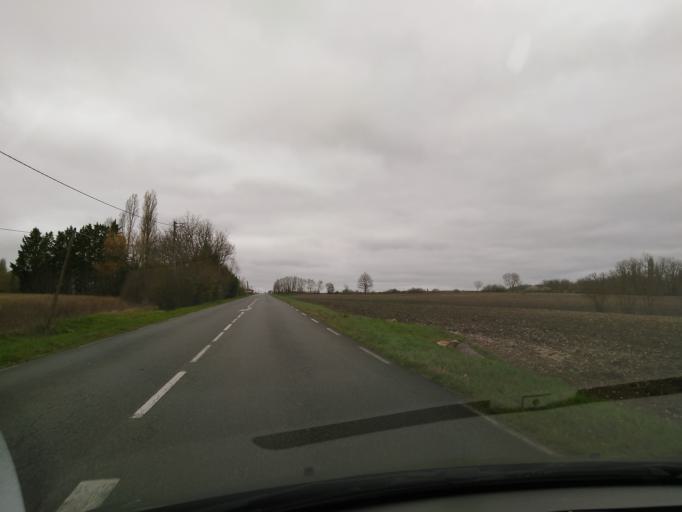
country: FR
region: Aquitaine
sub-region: Departement du Lot-et-Garonne
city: Castillonnes
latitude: 44.6892
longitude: 0.5703
